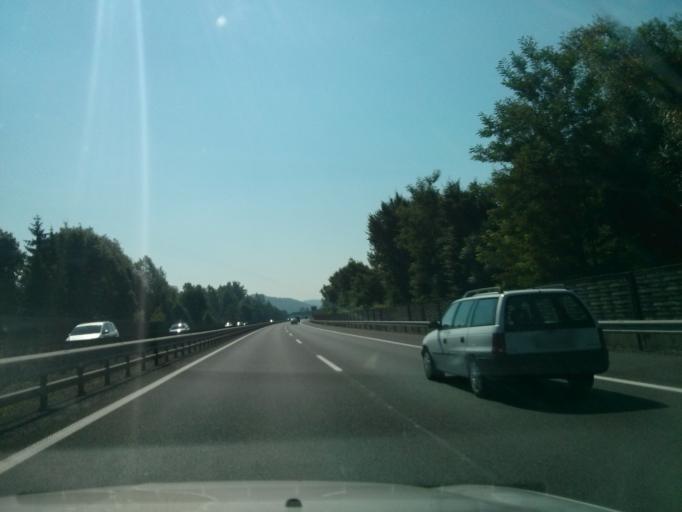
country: SI
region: Ljubljana
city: Ljubljana
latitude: 46.0223
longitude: 14.5119
